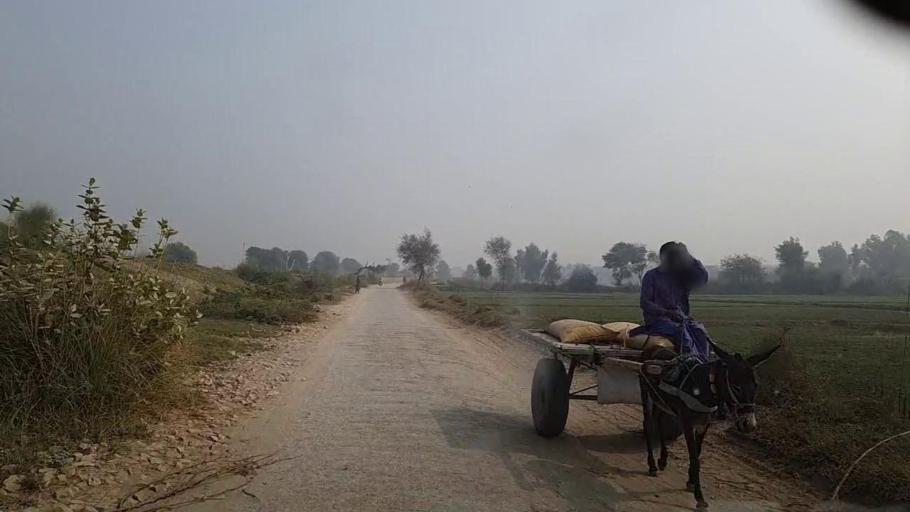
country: PK
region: Sindh
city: Bozdar
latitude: 27.0622
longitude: 68.6070
